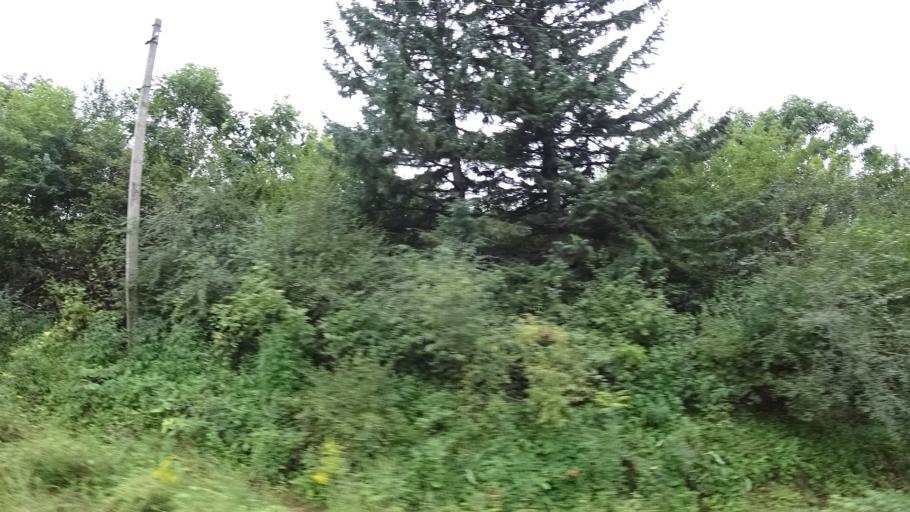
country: RU
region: Primorskiy
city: Rettikhovka
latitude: 44.1617
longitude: 132.7430
